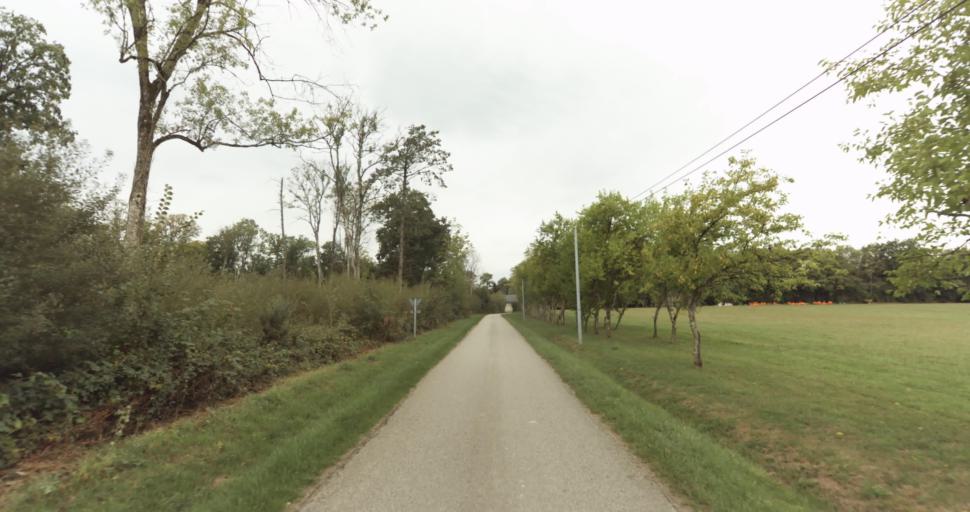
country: FR
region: Lower Normandy
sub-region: Departement de l'Orne
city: Sainte-Gauburge-Sainte-Colombe
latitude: 48.7494
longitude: 0.3611
